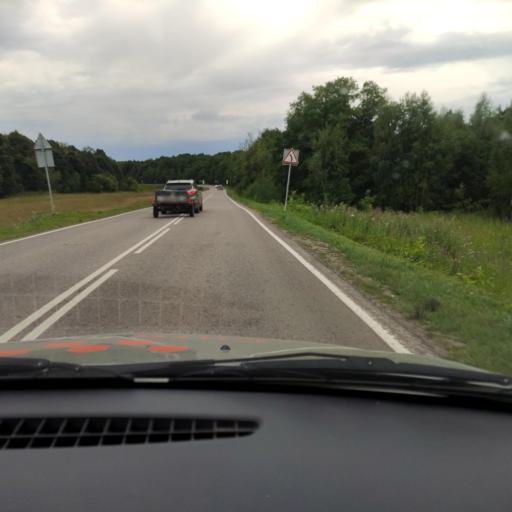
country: RU
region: Bashkortostan
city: Krasnaya Gorka
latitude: 55.2603
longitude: 56.6662
